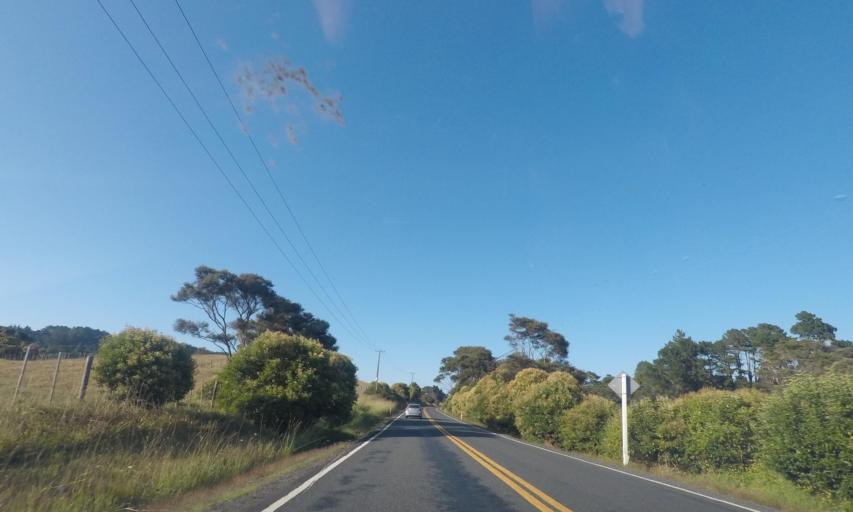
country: NZ
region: Auckland
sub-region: Auckland
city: Muriwai Beach
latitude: -36.7807
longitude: 174.4822
